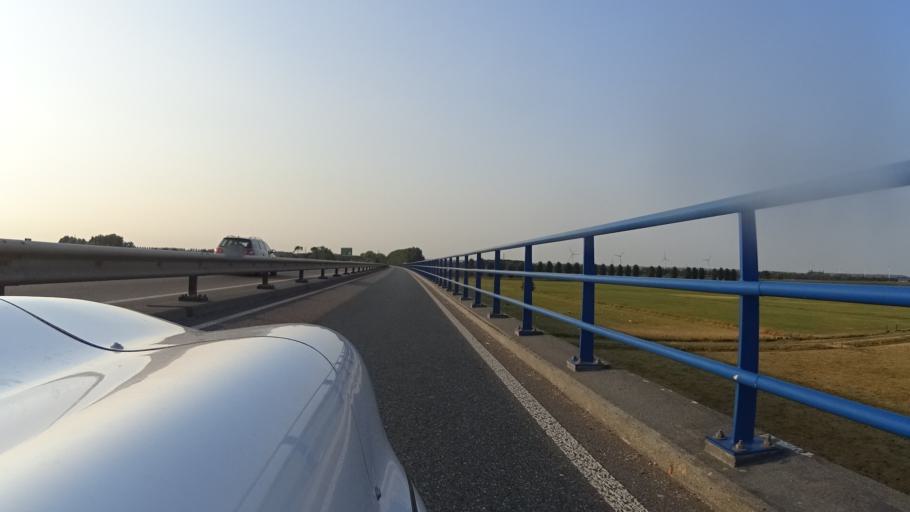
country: NL
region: Gelderland
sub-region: Gemeente Buren
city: Lienden
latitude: 51.8941
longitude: 5.4976
